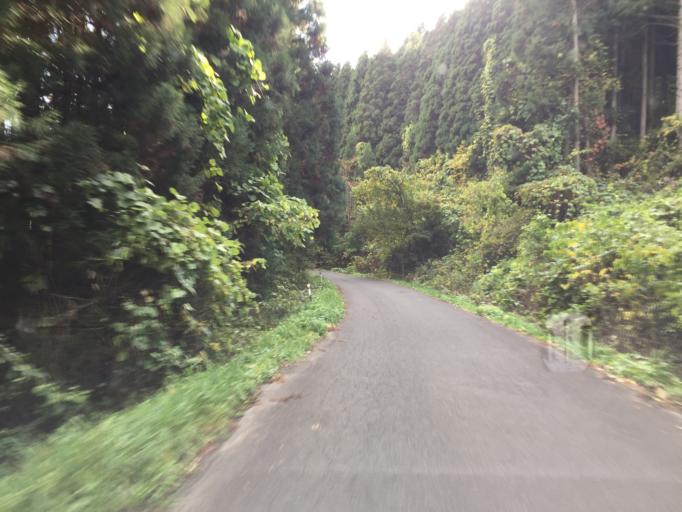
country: JP
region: Fukushima
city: Fukushima-shi
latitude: 37.7107
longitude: 140.3328
